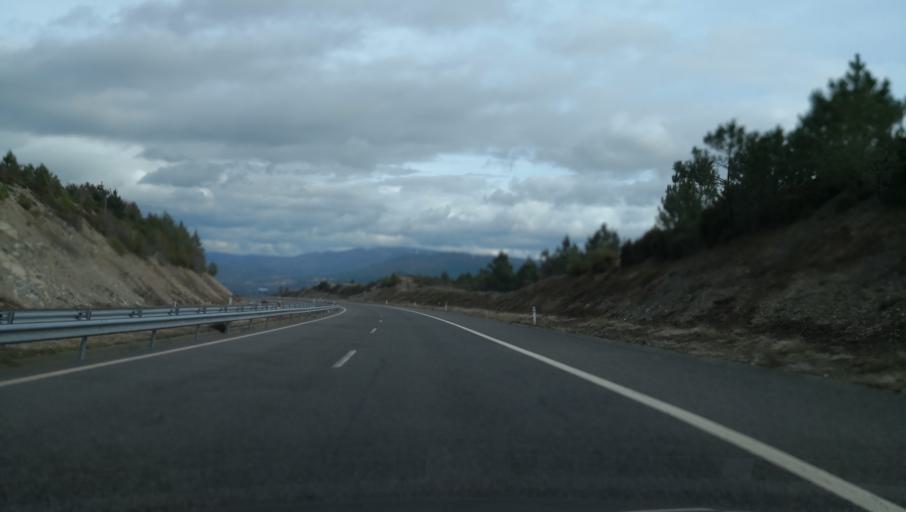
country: PT
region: Vila Real
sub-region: Vila Pouca de Aguiar
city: Vila Pouca de Aguiar
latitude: 41.5183
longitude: -7.6491
